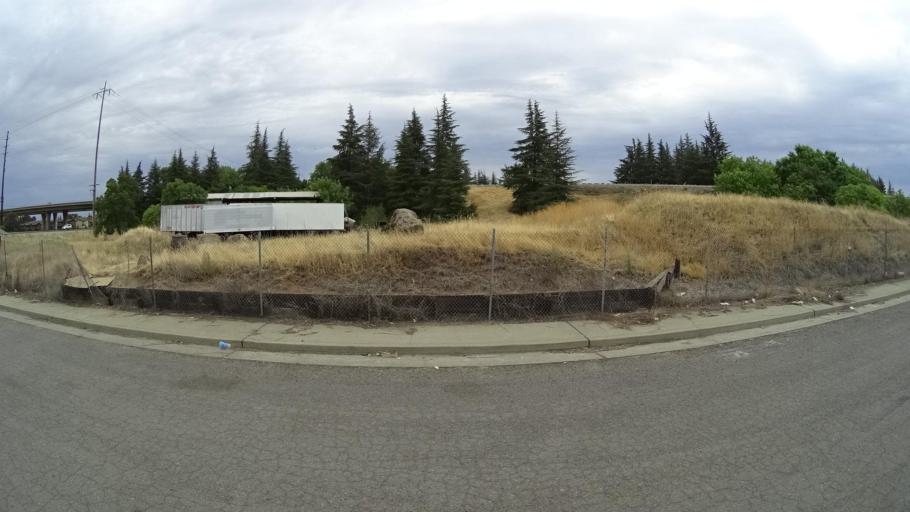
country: US
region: California
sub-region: Placer County
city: Rocklin
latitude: 38.7702
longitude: -121.2520
